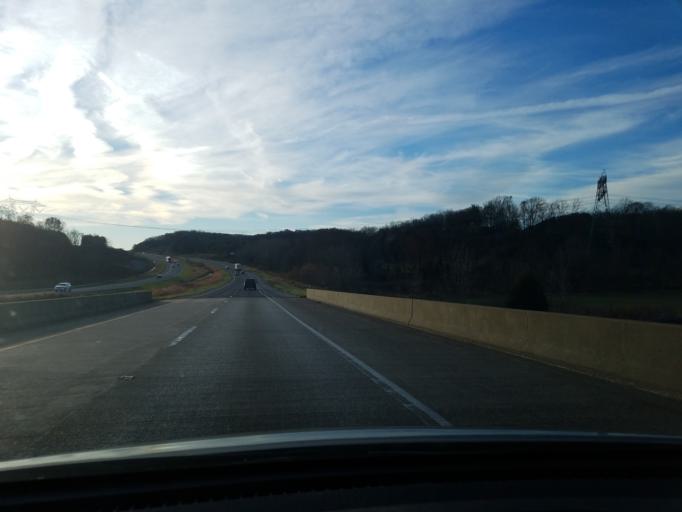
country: US
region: Indiana
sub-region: Dubois County
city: Ferdinand
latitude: 38.2165
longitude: -86.7342
